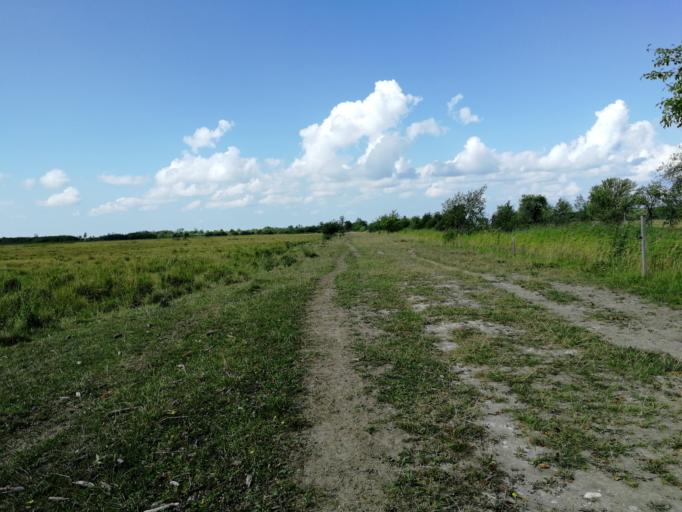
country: EE
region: Laeaene
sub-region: Lihula vald
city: Lihula
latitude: 58.7206
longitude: 23.8087
